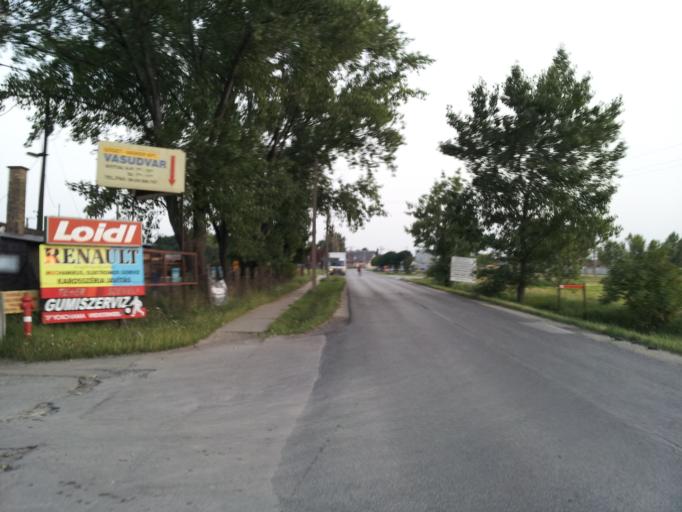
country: HU
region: Pest
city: Szigetszentmiklos
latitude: 47.3588
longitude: 19.0473
